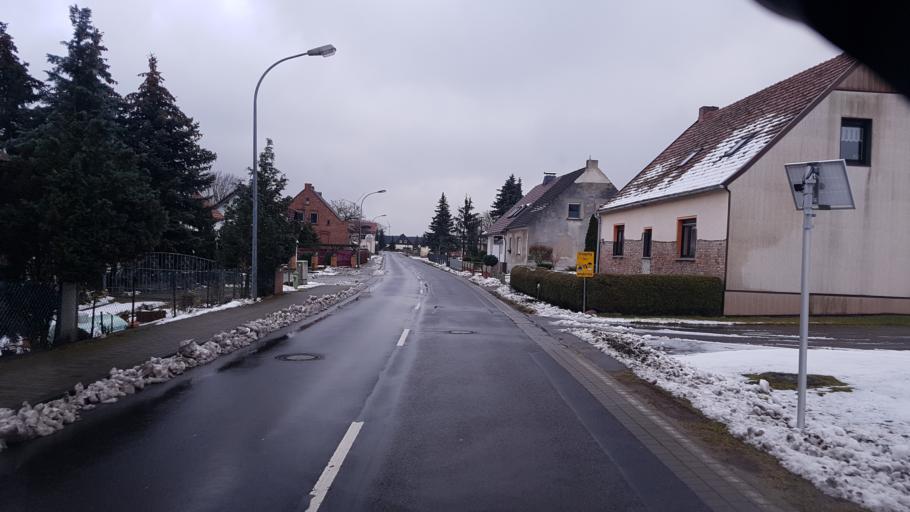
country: DE
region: Brandenburg
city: Schenkendobern
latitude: 51.9712
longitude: 14.5682
